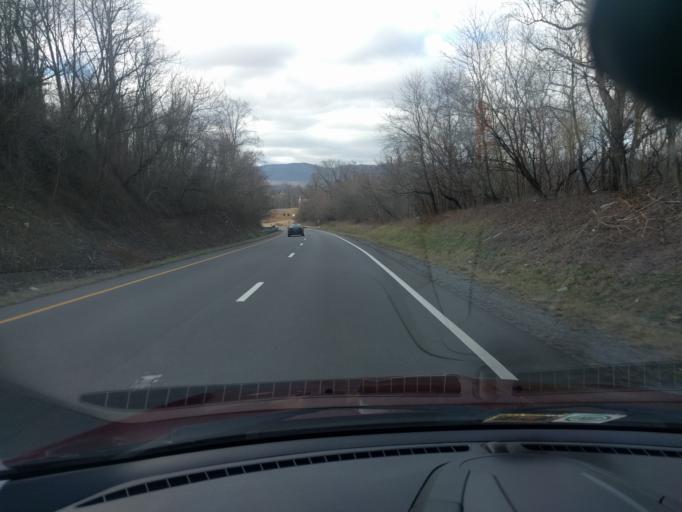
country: US
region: Virginia
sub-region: Botetourt County
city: Blue Ridge
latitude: 37.3674
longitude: -79.6921
